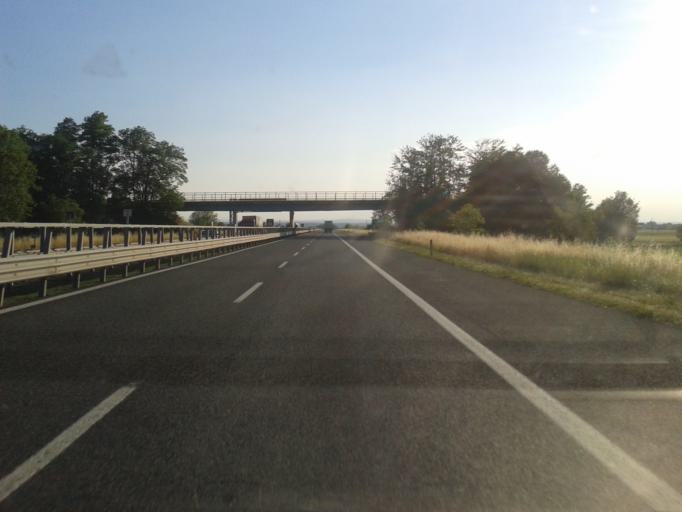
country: IT
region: Piedmont
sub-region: Provincia di Alessandria
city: Basaluzzo
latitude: 44.7822
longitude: 8.7100
